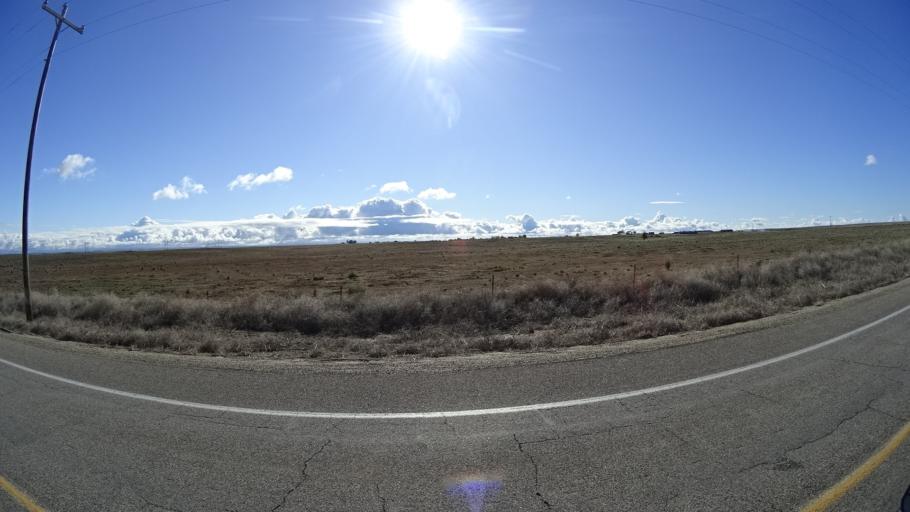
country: US
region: Idaho
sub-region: Ada County
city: Kuna
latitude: 43.4184
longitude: -116.4140
